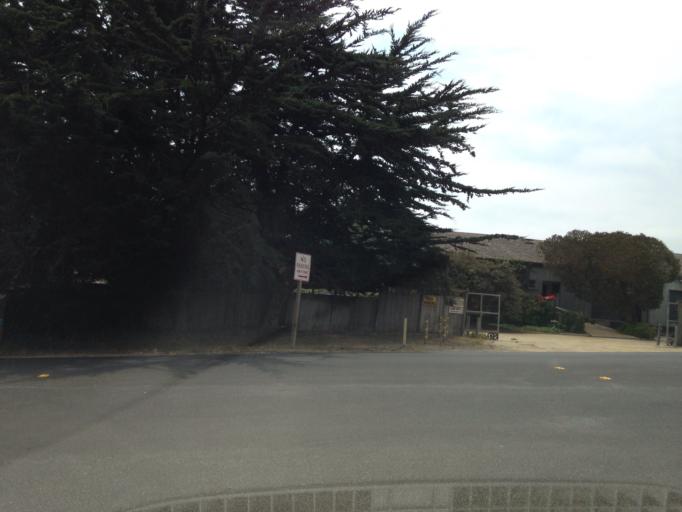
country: US
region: California
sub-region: Santa Cruz County
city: Bonny Doon
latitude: 37.0106
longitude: -122.1938
